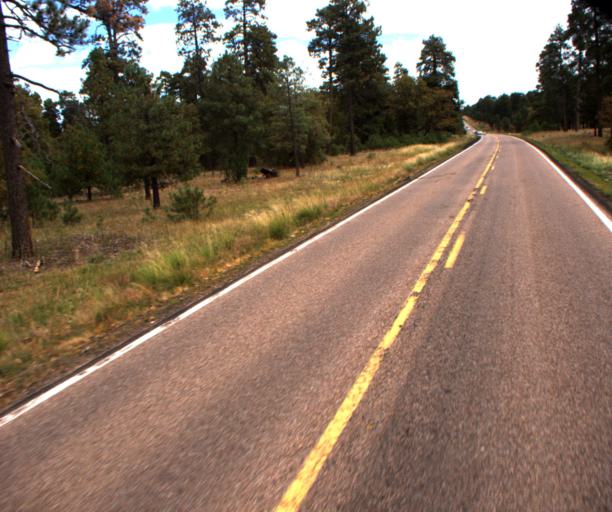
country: US
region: Arizona
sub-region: Navajo County
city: Heber-Overgaard
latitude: 34.3383
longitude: -110.7310
